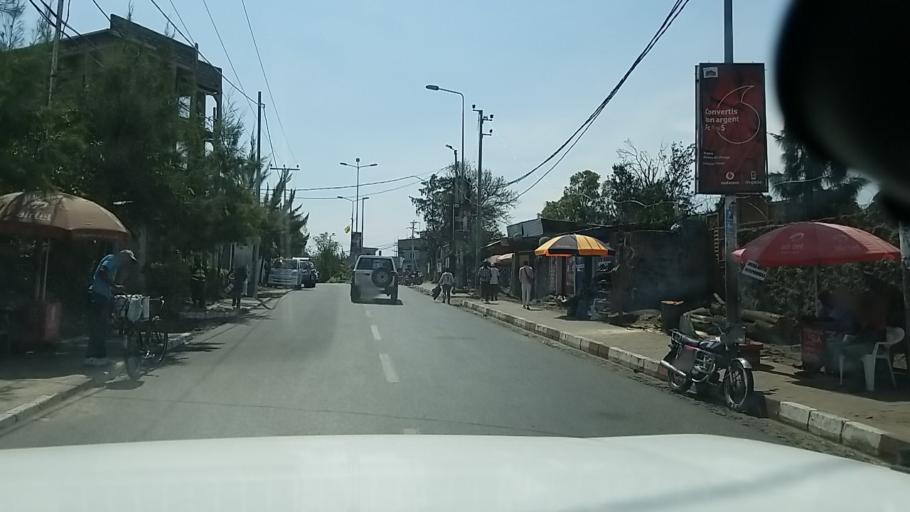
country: RW
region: Western Province
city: Gisenyi
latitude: -1.6979
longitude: 29.2416
